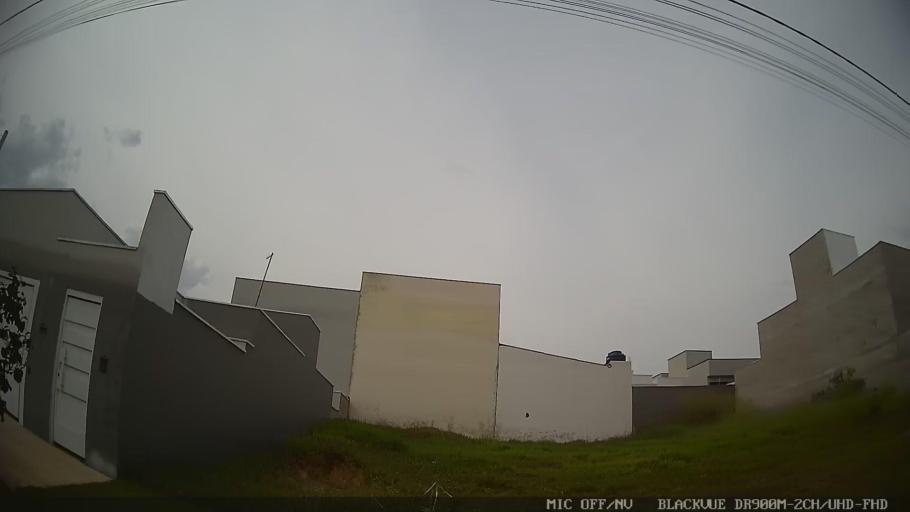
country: BR
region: Sao Paulo
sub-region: Indaiatuba
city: Indaiatuba
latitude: -23.0983
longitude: -47.2536
